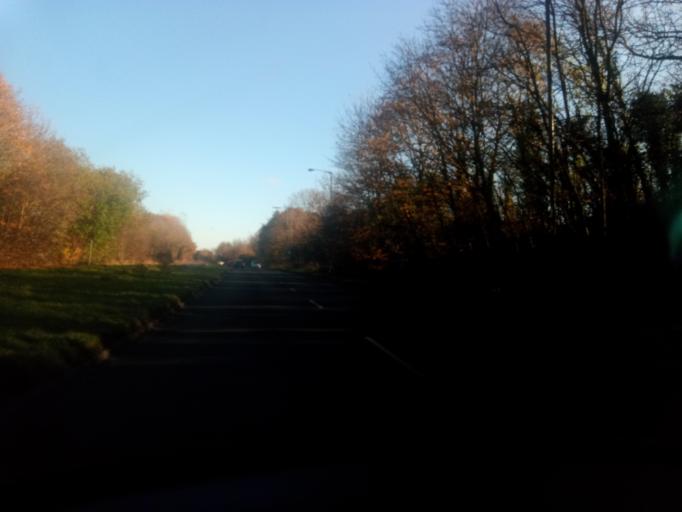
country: GB
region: England
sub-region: Derbyshire
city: Heage
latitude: 53.0604
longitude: -1.4346
